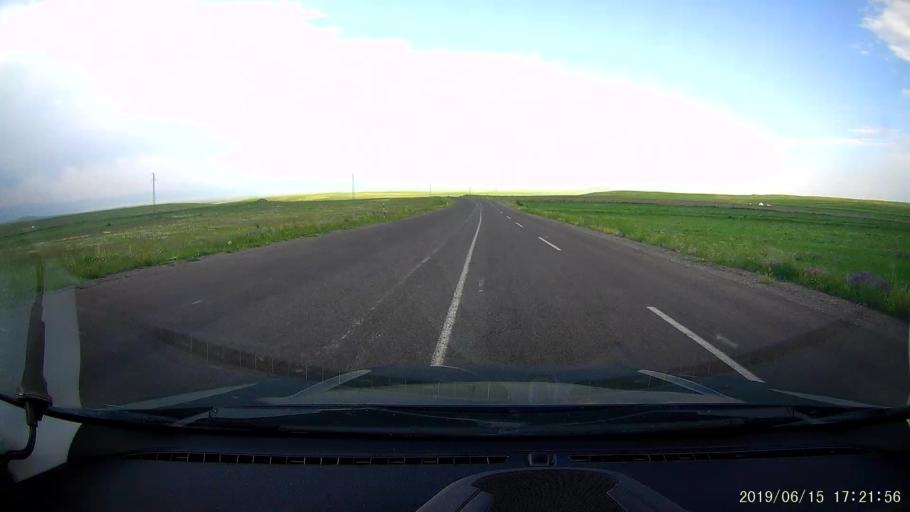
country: TR
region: Kars
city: Basgedikler
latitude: 40.6175
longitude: 43.3336
